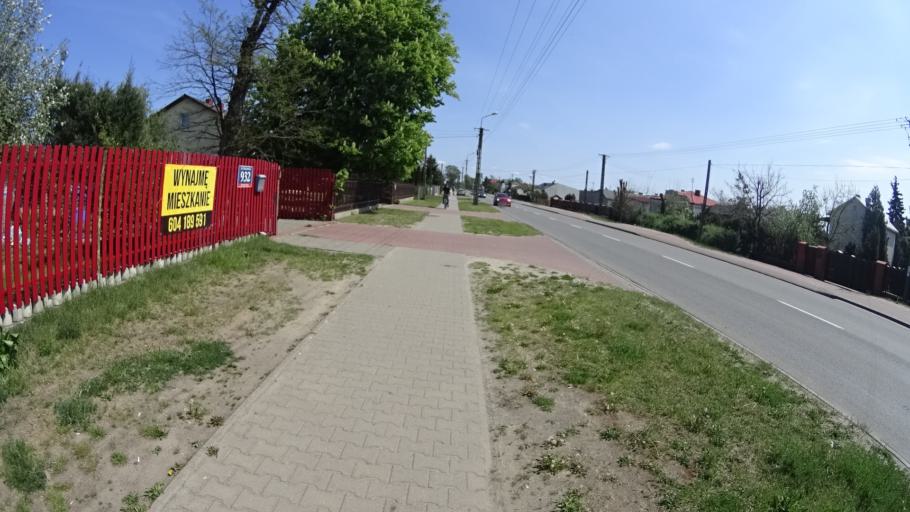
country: PL
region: Masovian Voivodeship
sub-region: Powiat warszawski zachodni
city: Jozefow
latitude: 52.2556
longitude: 20.7200
